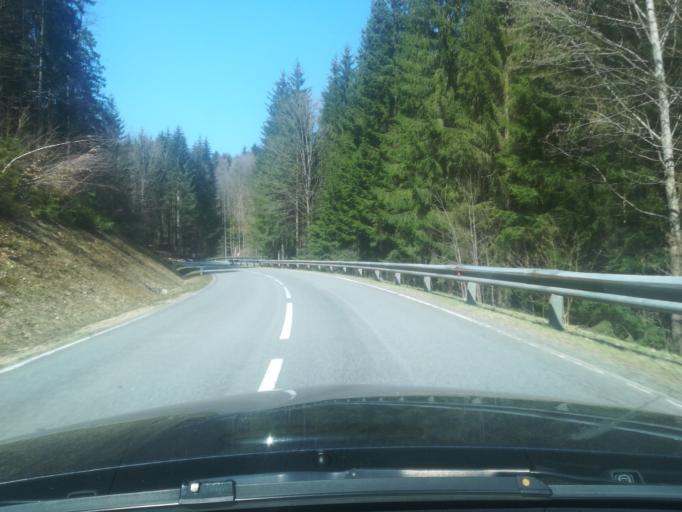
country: AT
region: Upper Austria
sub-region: Politischer Bezirk Perg
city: Sankt Georgen am Walde
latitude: 48.4195
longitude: 14.7637
